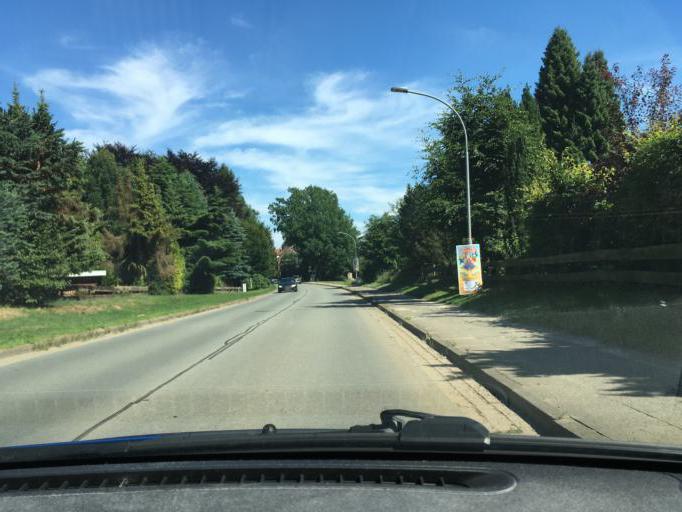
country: DE
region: Lower Saxony
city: Bendestorf
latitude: 53.3687
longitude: 9.9162
